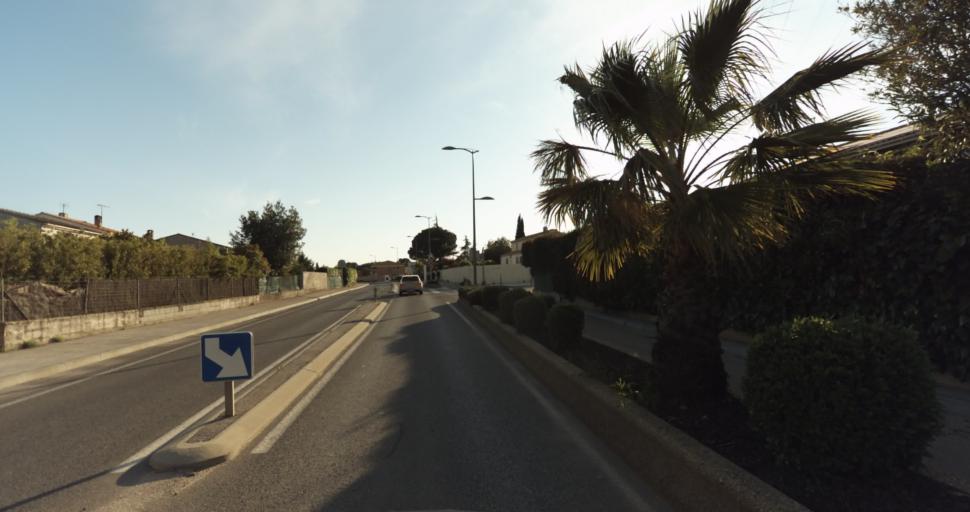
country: FR
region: Provence-Alpes-Cote d'Azur
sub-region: Departement du Var
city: La Crau
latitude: 43.1536
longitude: 6.0856
